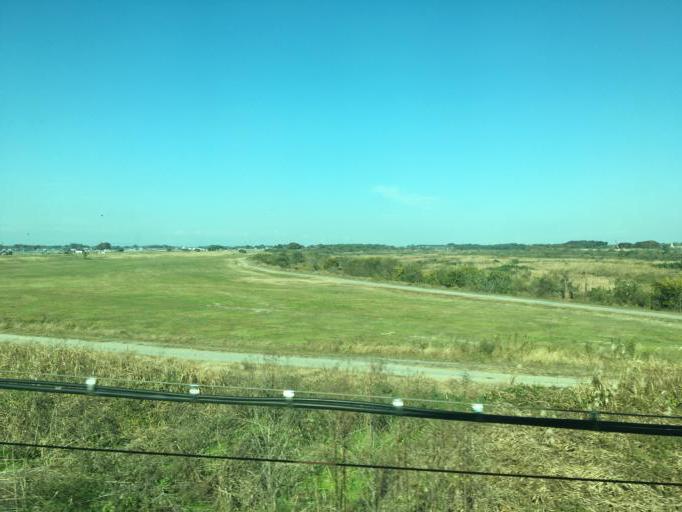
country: JP
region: Ibaraki
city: Yuki
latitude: 36.2963
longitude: 139.9061
